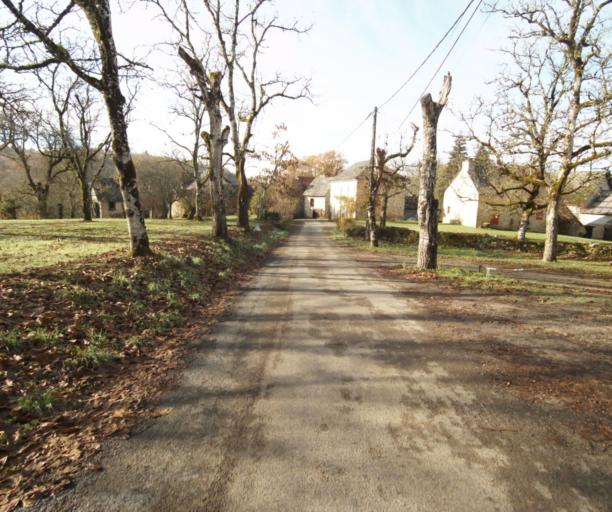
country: FR
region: Limousin
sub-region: Departement de la Correze
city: Chameyrat
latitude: 45.2257
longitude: 1.7364
